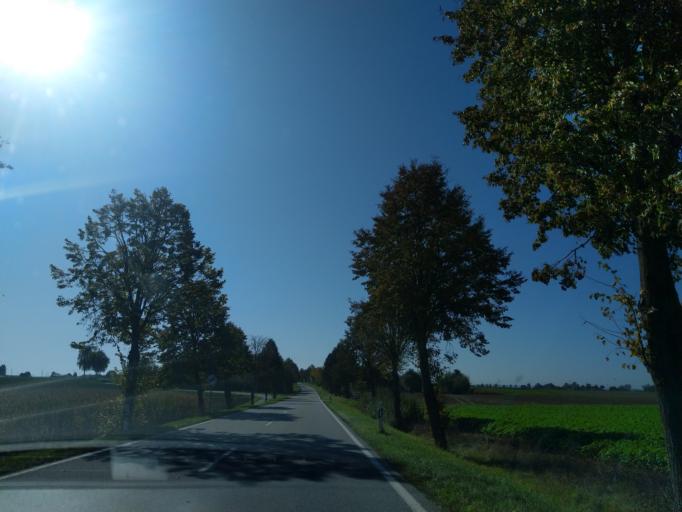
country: DE
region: Bavaria
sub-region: Lower Bavaria
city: Stephansposching
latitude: 48.8124
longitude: 12.8012
